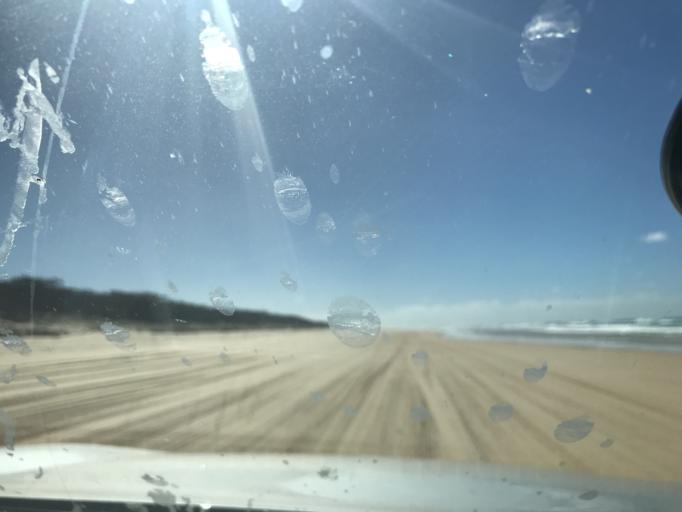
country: AU
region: Queensland
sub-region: Fraser Coast
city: Urangan
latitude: -25.0441
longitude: 153.3440
